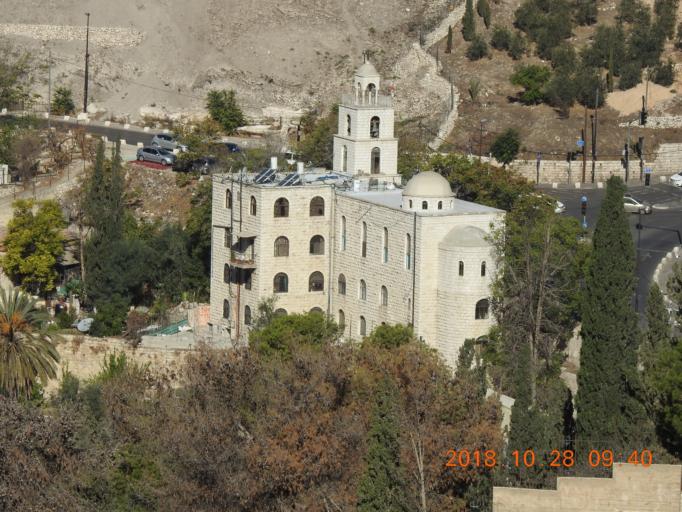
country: PS
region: West Bank
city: Old City
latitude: 31.7763
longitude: 35.2431
